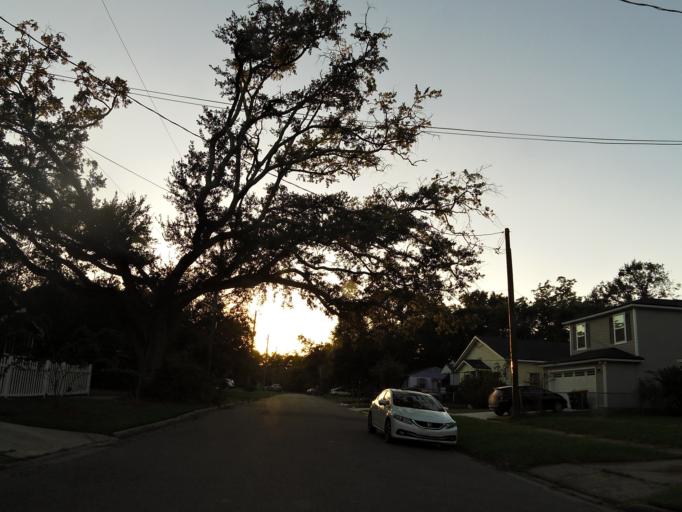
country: US
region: Florida
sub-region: Duval County
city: Jacksonville
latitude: 30.3147
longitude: -81.7118
